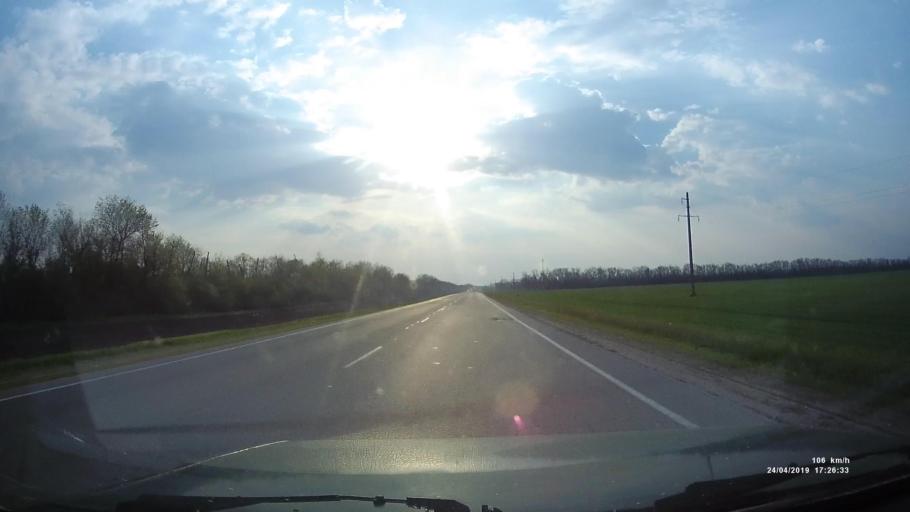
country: RU
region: Rostov
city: Gigant
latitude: 46.5276
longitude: 41.2175
